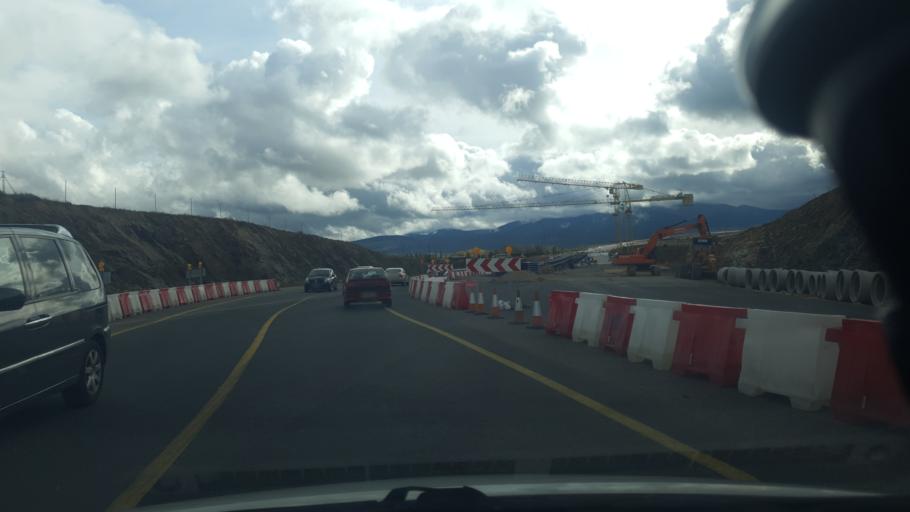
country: ES
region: Castille and Leon
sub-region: Provincia de Segovia
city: San Cristobal de Segovia
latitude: 40.9420
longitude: -4.0856
